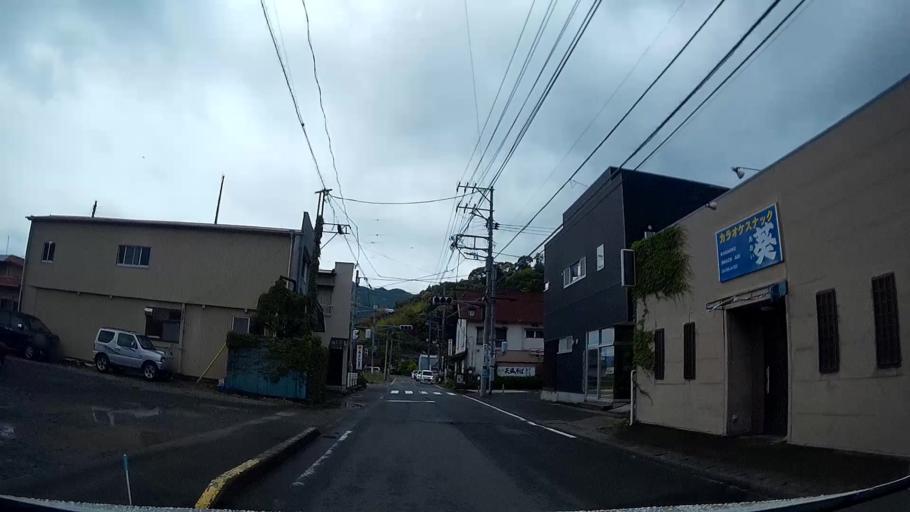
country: JP
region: Shizuoka
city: Shimoda
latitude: 34.7560
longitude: 138.9838
